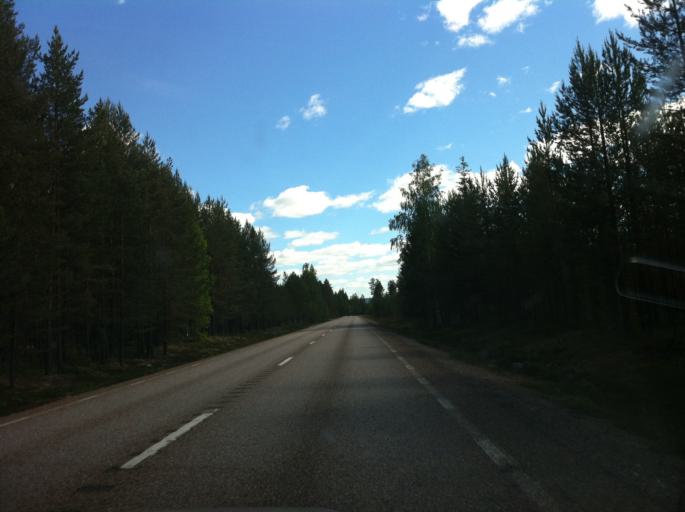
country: SE
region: Gaevleborg
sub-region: Ljusdals Kommun
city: Farila
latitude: 61.9698
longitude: 15.3486
